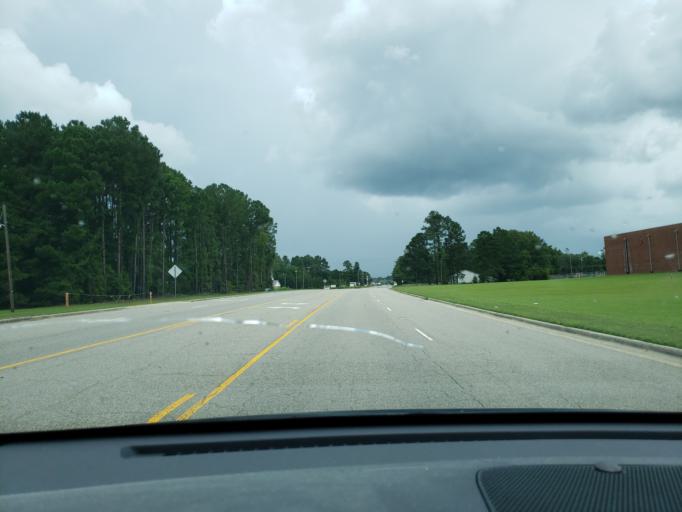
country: US
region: North Carolina
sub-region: Bladen County
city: Bladenboro
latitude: 34.4846
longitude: -78.6644
